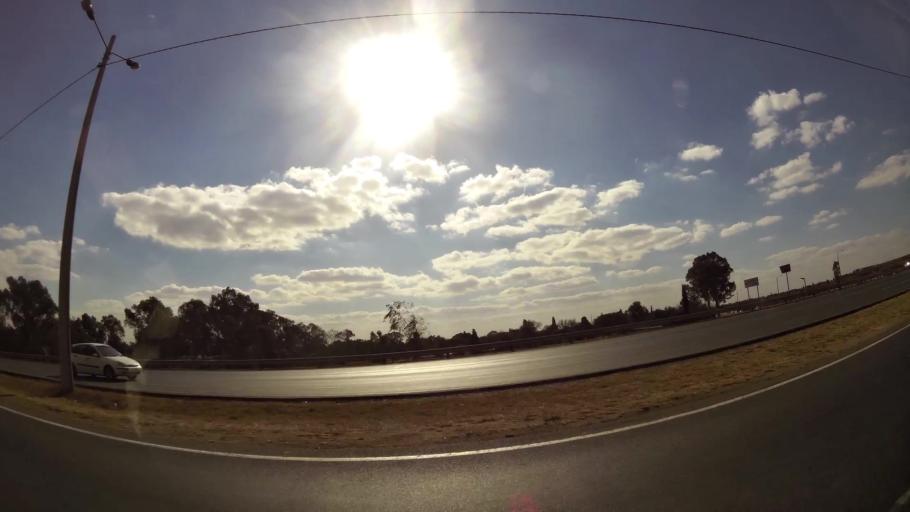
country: ZA
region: Gauteng
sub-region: Ekurhuleni Metropolitan Municipality
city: Tembisa
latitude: -25.9741
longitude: 28.2436
